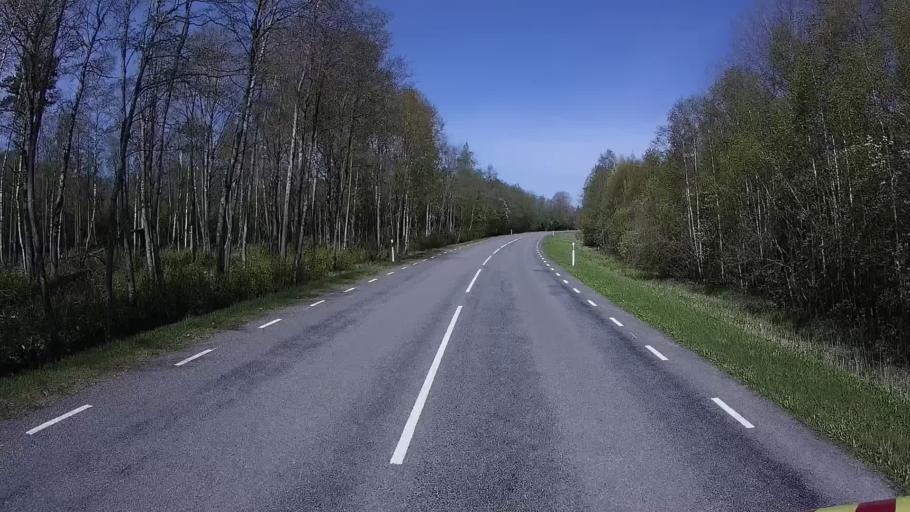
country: EE
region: Laeaene
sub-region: Lihula vald
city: Lihula
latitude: 58.6498
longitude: 23.8410
